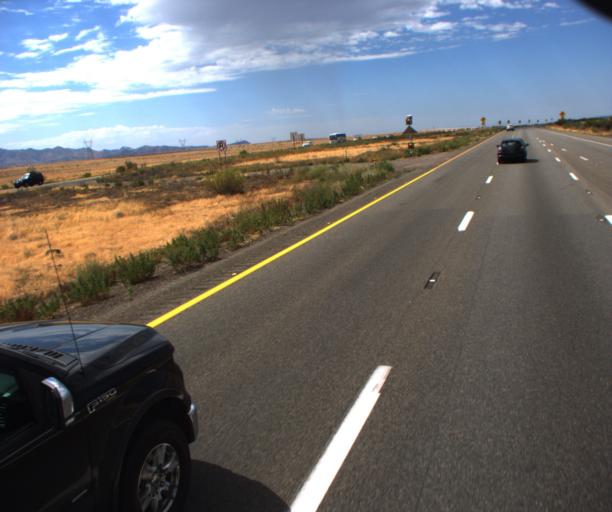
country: US
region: Arizona
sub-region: Yavapai County
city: Black Canyon City
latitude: 34.1792
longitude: -112.1352
